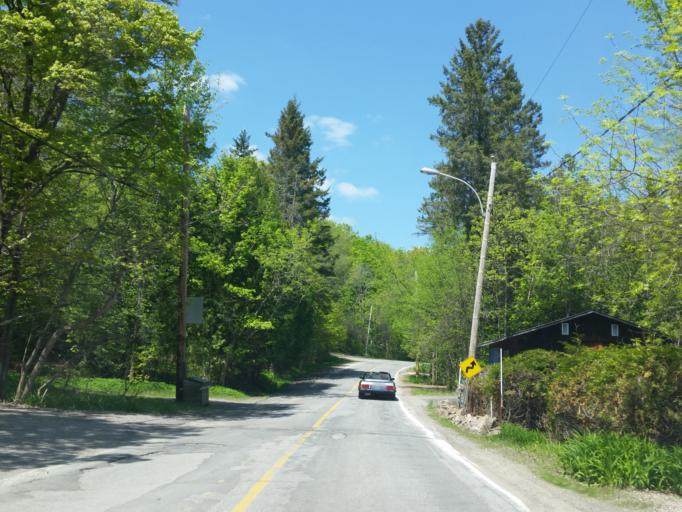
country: CA
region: Quebec
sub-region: Outaouais
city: Wakefield
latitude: 45.5887
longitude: -75.8698
